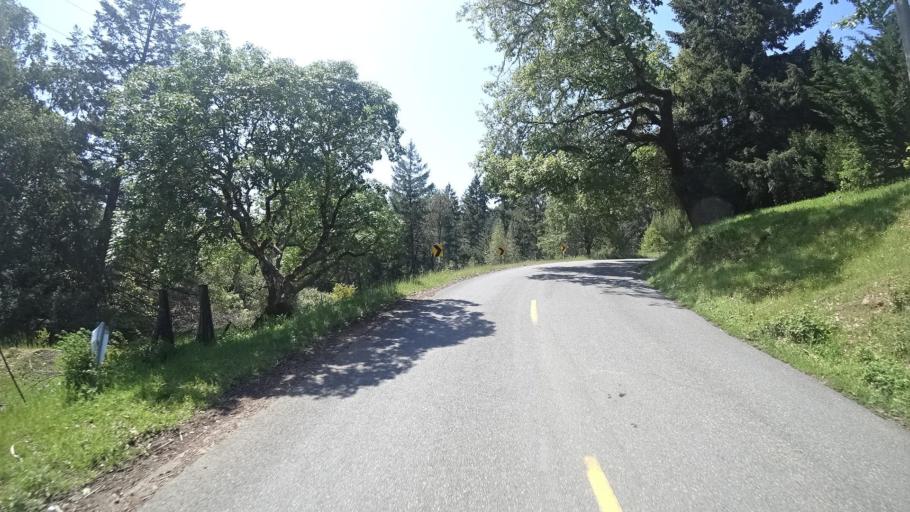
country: US
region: California
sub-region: Humboldt County
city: Redway
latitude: 40.1510
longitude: -123.6248
